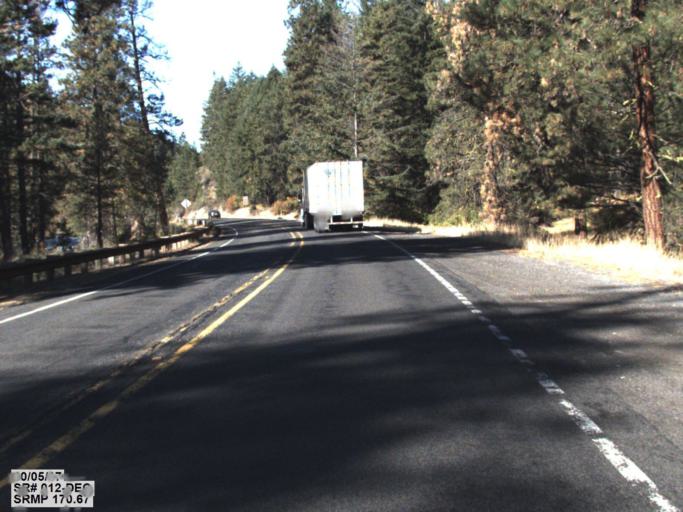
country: US
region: Washington
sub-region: Yakima County
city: Tieton
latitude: 46.6725
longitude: -121.0323
